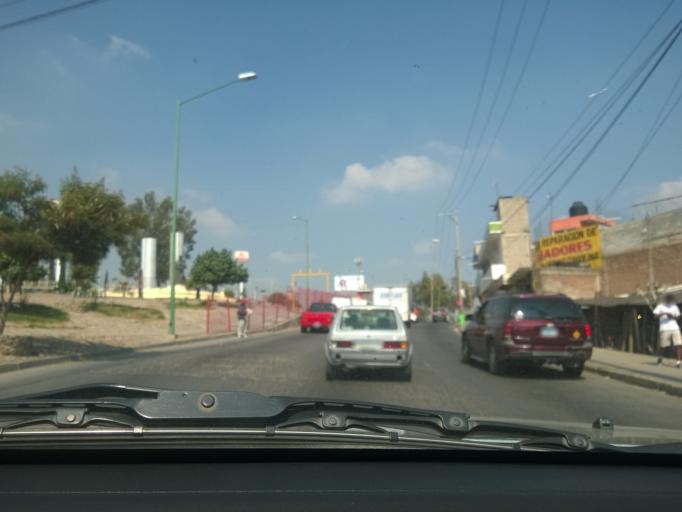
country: MX
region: Guanajuato
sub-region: Leon
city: La Ermita
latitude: 21.1331
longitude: -101.7143
